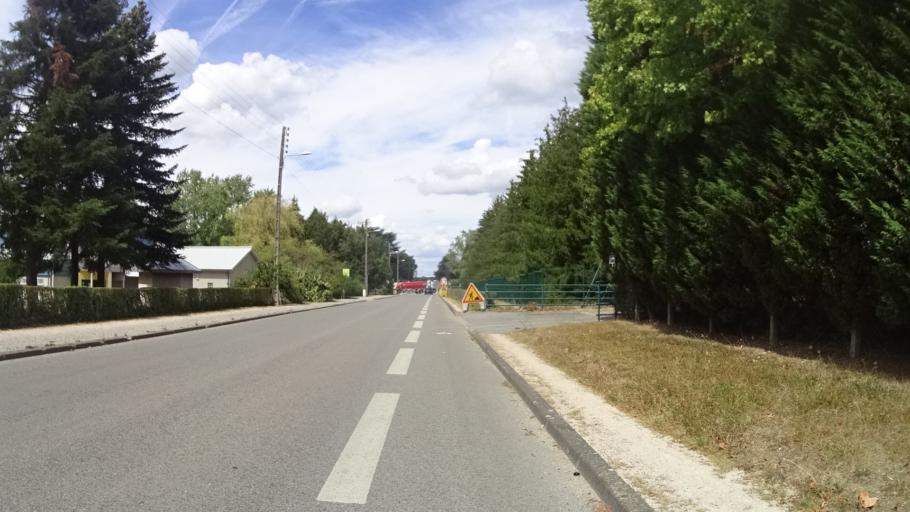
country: FR
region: Franche-Comte
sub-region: Departement du Jura
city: Damparis
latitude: 47.0654
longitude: 5.4154
